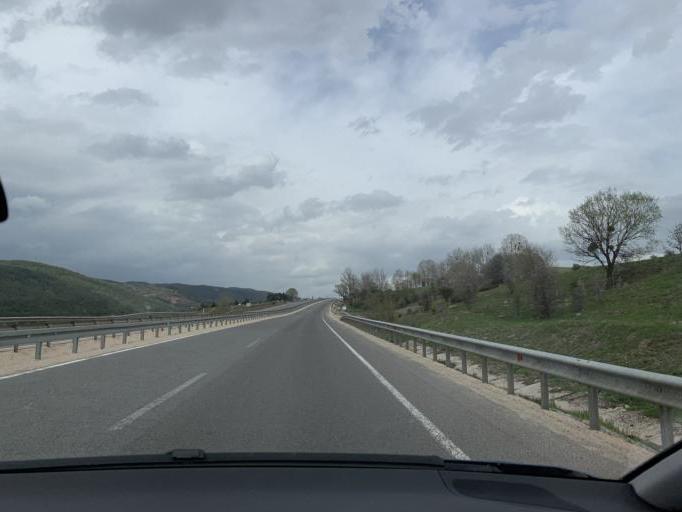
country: TR
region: Bolu
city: Gerede
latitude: 40.7904
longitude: 32.1332
